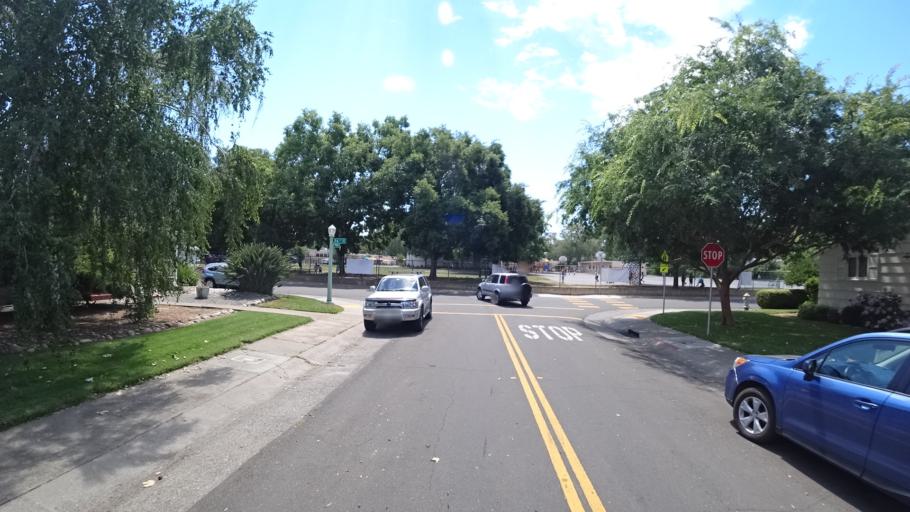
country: US
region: California
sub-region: Sacramento County
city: Sacramento
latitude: 38.5785
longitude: -121.4524
